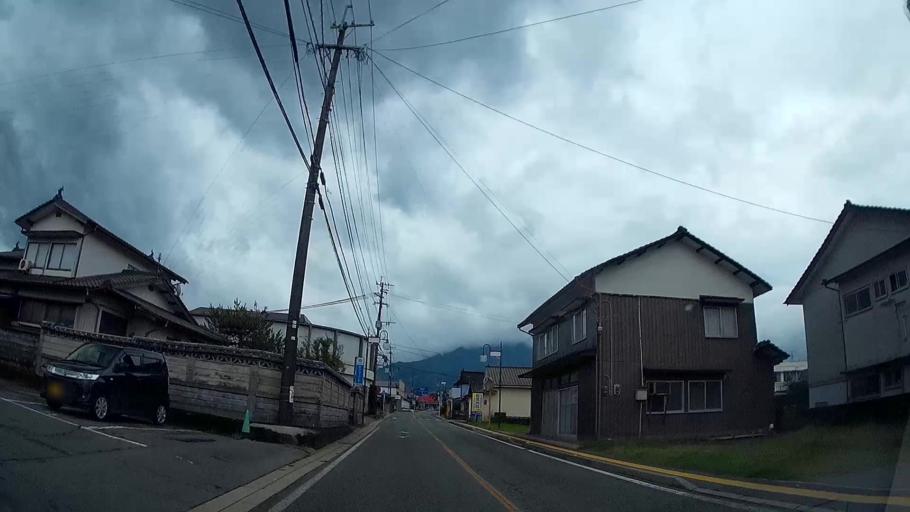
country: JP
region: Kumamoto
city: Aso
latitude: 32.9402
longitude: 131.1175
